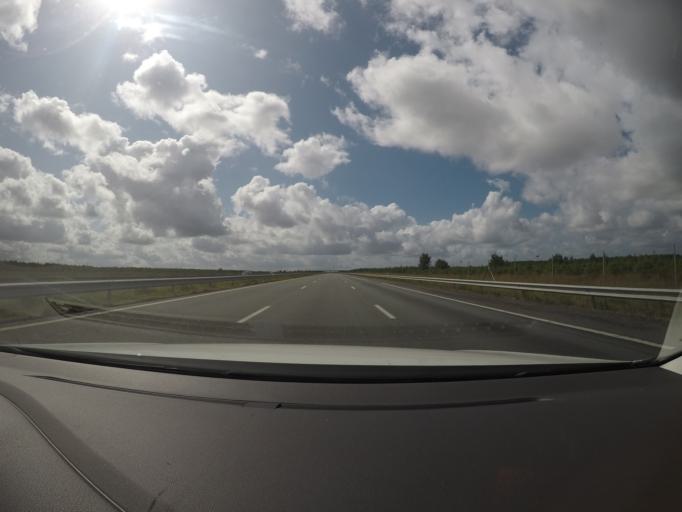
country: FR
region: Aquitaine
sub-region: Departement des Landes
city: Labouheyre
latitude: 44.1890
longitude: -0.9384
